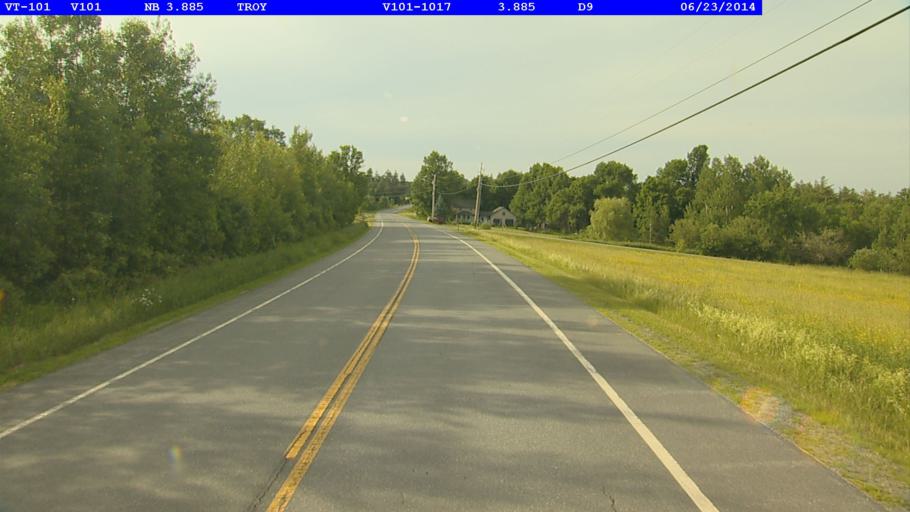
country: US
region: Vermont
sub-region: Orleans County
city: Newport
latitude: 44.9585
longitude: -72.4125
